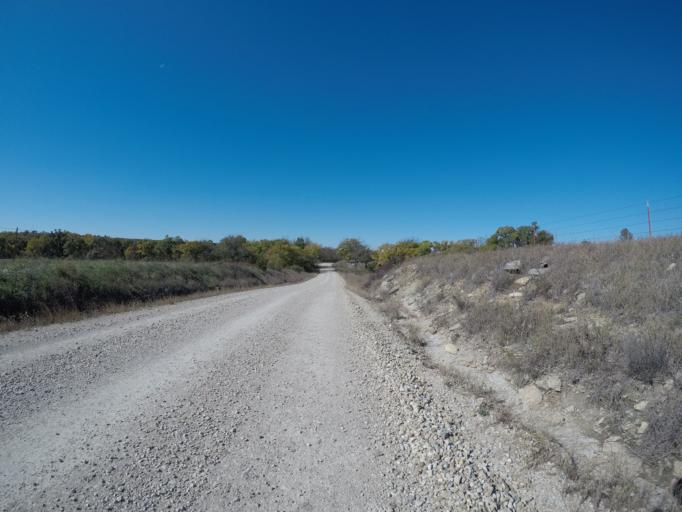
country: US
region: Kansas
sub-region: Wabaunsee County
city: Alma
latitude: 38.9762
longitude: -96.3680
